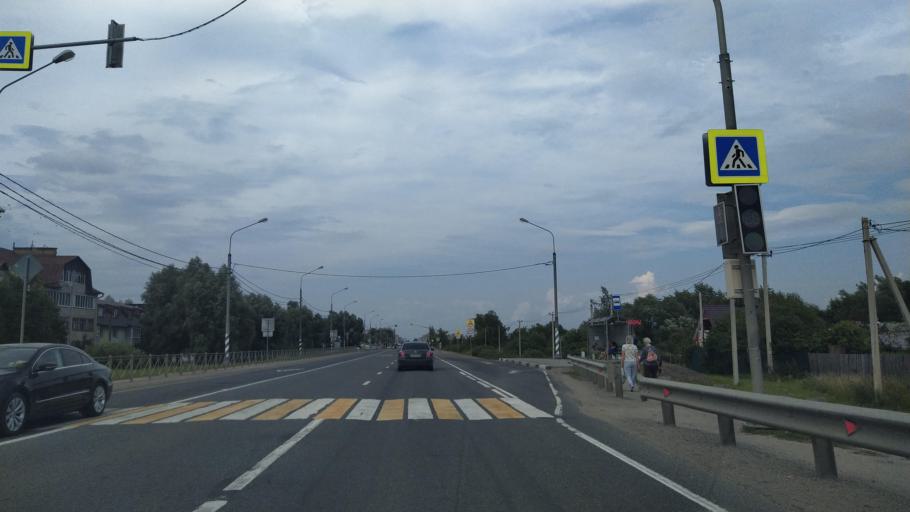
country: RU
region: Novgorod
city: Pankovka
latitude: 58.4952
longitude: 31.2103
